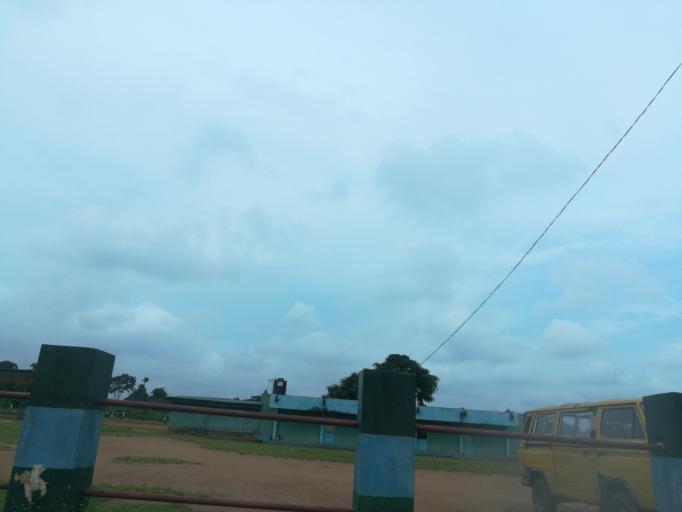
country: NG
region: Lagos
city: Oshodi
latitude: 6.5645
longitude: 3.3575
